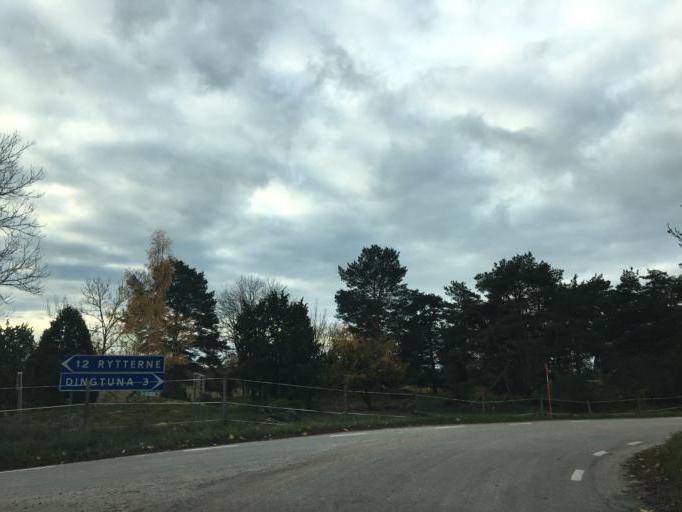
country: SE
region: Vaestmanland
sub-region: Vasteras
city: Vasteras
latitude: 59.5648
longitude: 16.4329
